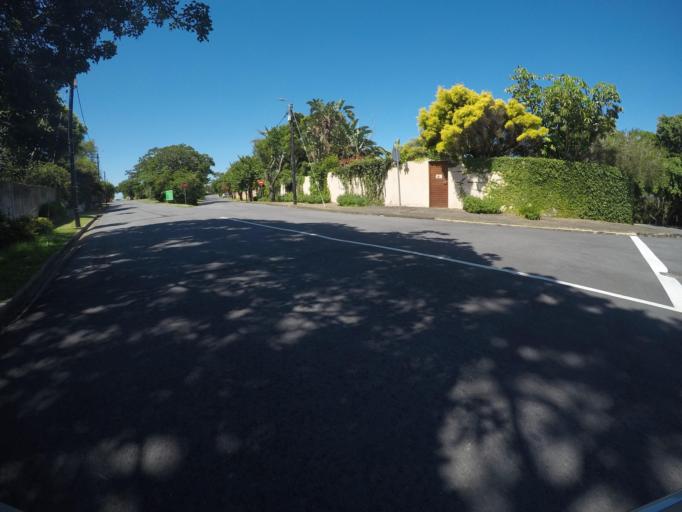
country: ZA
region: Eastern Cape
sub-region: Buffalo City Metropolitan Municipality
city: East London
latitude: -32.9799
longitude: 27.9242
